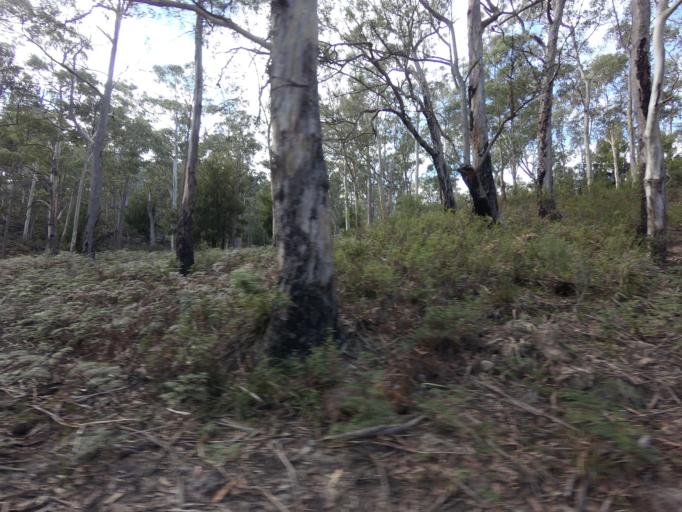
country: AU
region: Tasmania
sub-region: Clarence
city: Sandford
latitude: -43.0740
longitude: 147.6671
